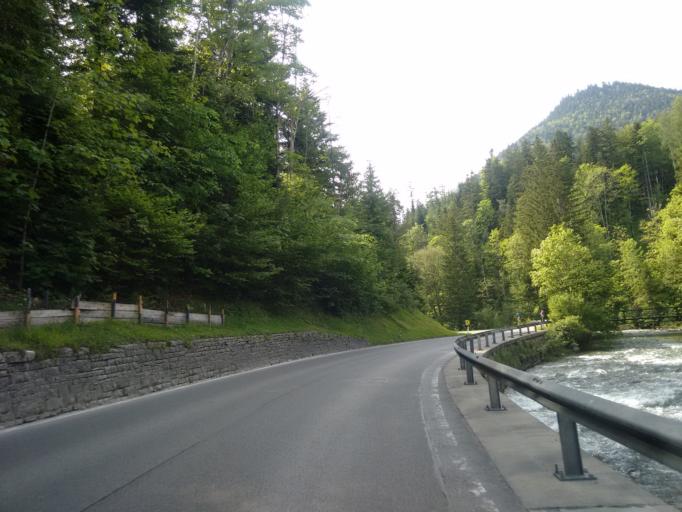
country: AT
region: Styria
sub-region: Politischer Bezirk Liezen
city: Bad Aussee
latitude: 47.6170
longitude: 13.8014
